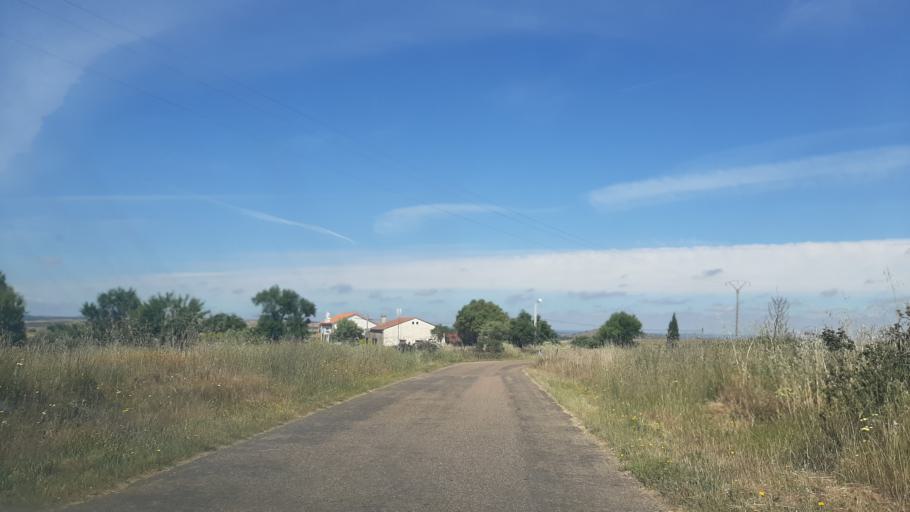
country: ES
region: Castille and Leon
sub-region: Provincia de Salamanca
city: Zamarra
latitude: 40.5208
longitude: -6.4509
